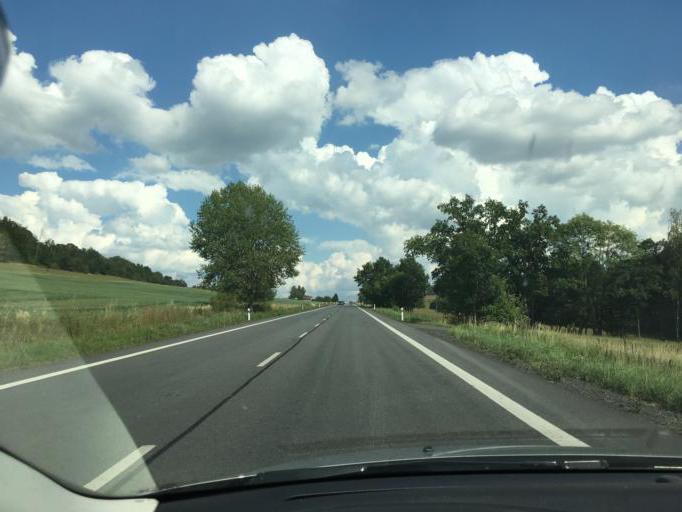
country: CZ
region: Liberecky
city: Jilemnice
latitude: 50.6228
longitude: 15.5384
